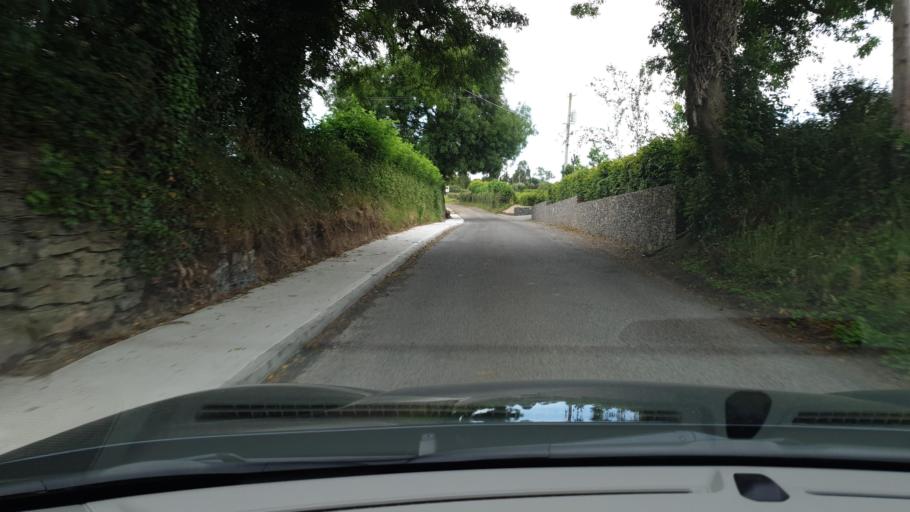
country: IE
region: Leinster
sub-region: An Mhi
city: Stamullin
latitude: 53.5880
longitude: -6.3390
